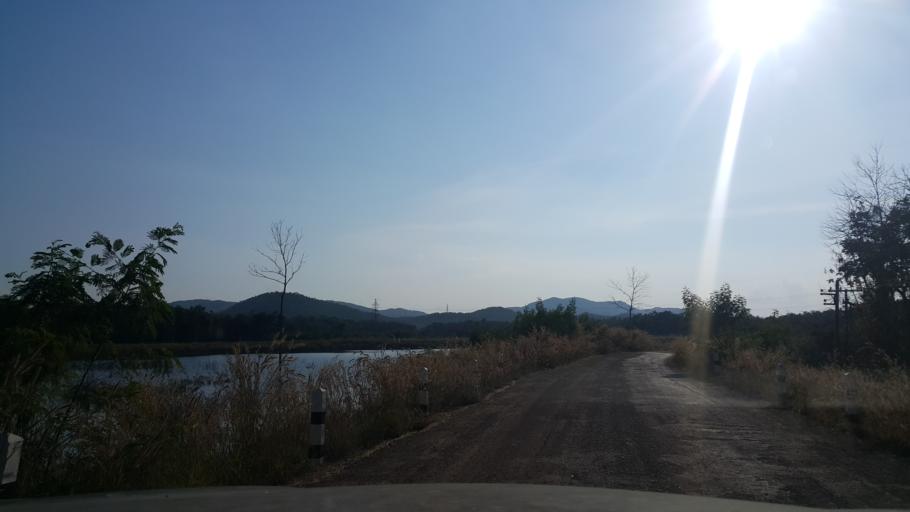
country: TH
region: Lamphun
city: Mae Tha
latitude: 18.5184
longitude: 99.1152
